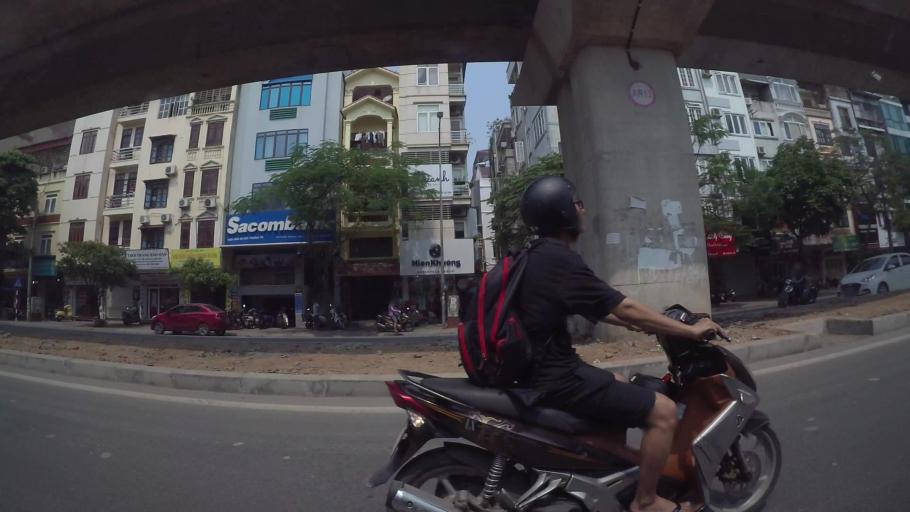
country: VN
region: Ha Noi
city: Dong Da
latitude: 21.0245
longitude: 105.8271
